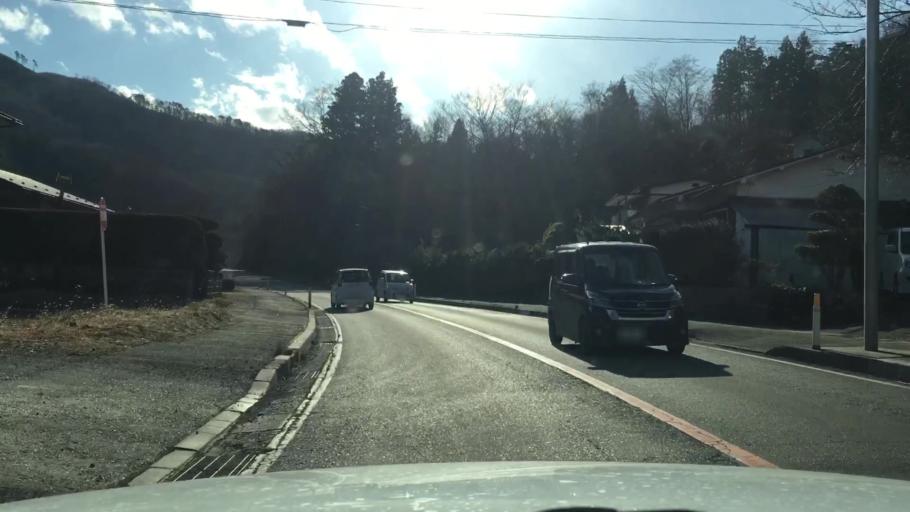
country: JP
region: Iwate
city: Miyako
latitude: 39.5982
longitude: 141.6777
